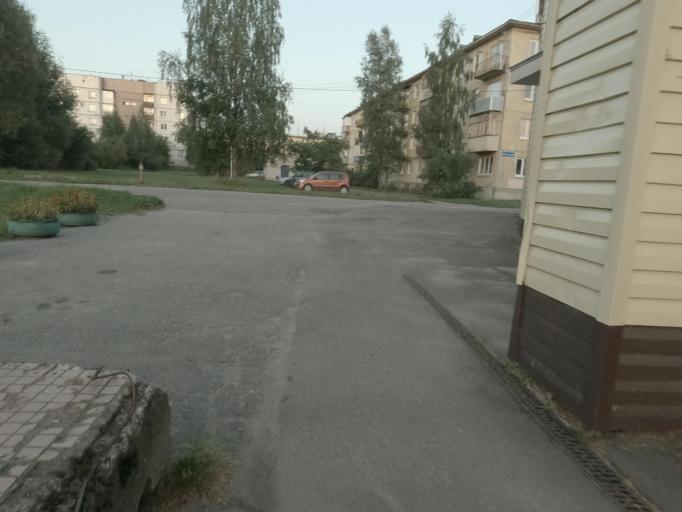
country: RU
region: Leningrad
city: Mga
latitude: 59.7600
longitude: 31.0614
